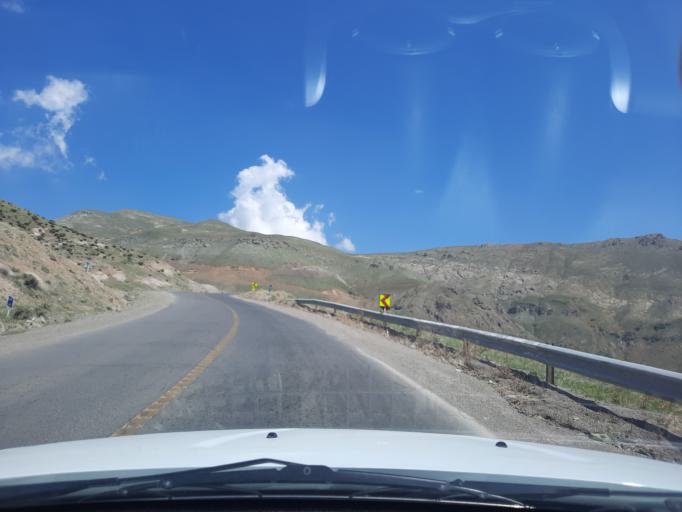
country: IR
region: Qazvin
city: Qazvin
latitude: 36.3675
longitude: 50.2024
